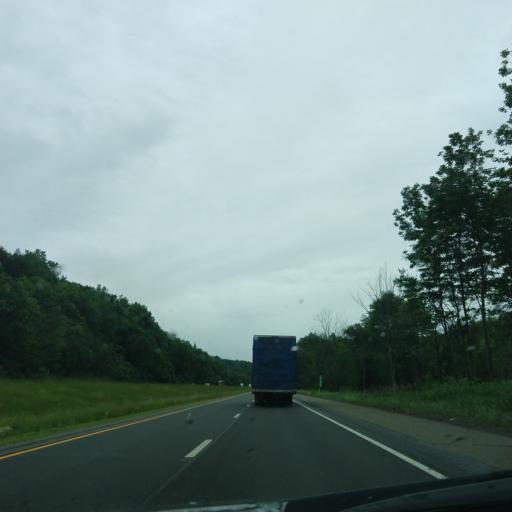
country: US
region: Pennsylvania
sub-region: Susquehanna County
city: Susquehanna
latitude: 41.7519
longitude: -75.6820
